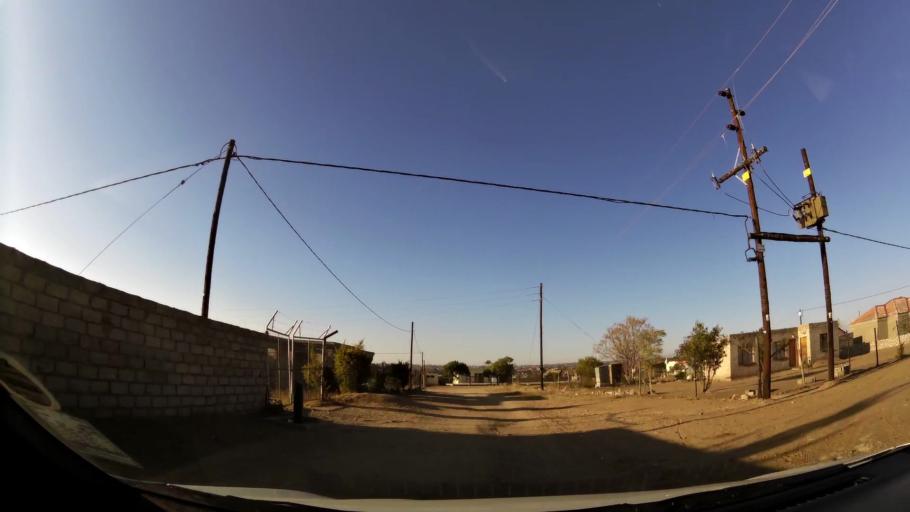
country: ZA
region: Limpopo
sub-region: Capricorn District Municipality
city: Polokwane
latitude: -23.8389
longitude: 29.3632
